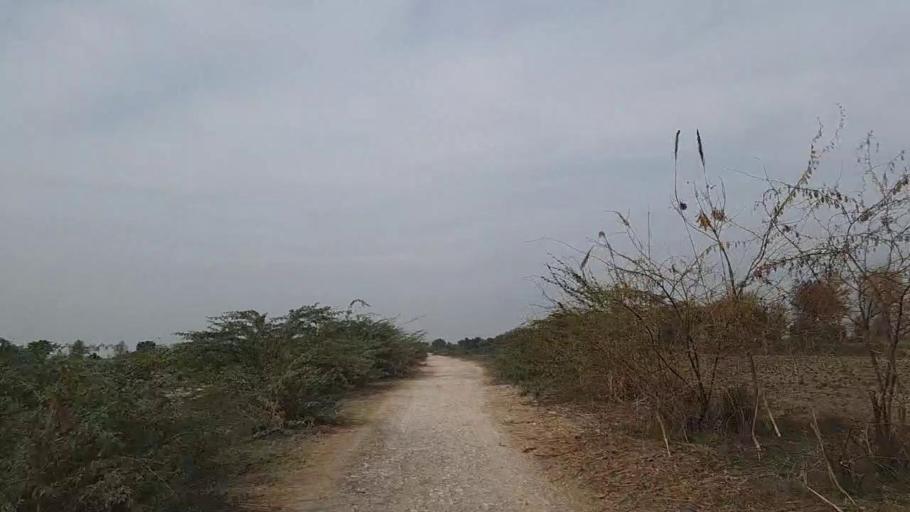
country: PK
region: Sindh
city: Daur
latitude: 26.4212
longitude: 68.4199
